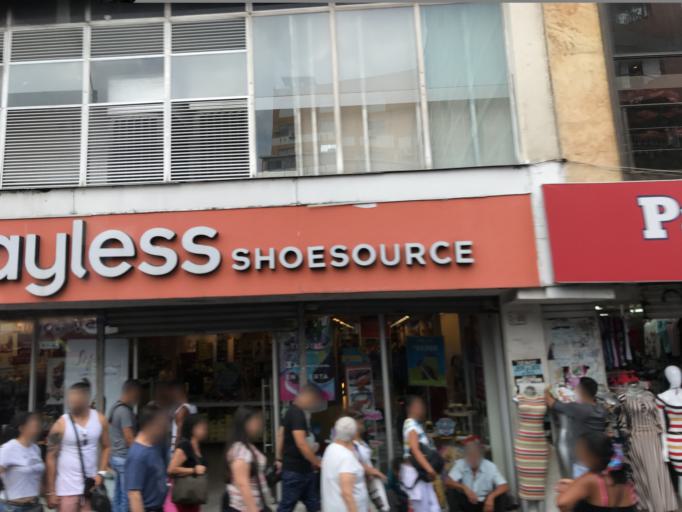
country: CO
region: Valle del Cauca
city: Cali
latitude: 3.4501
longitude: -76.5307
